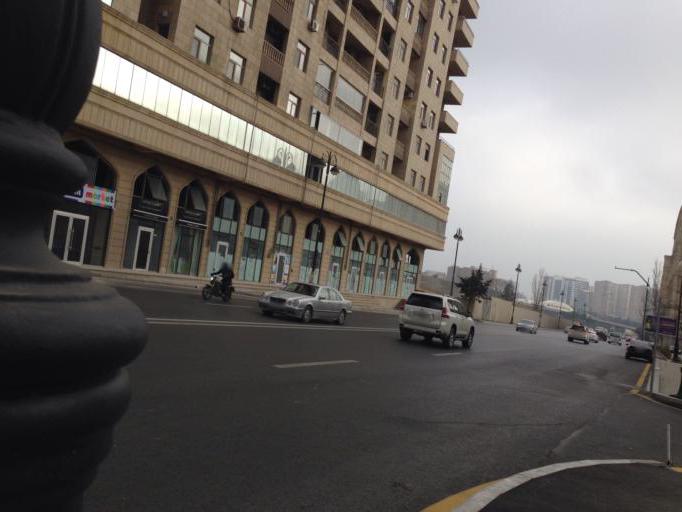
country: AZ
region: Baki
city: Baku
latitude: 40.3949
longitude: 49.8617
